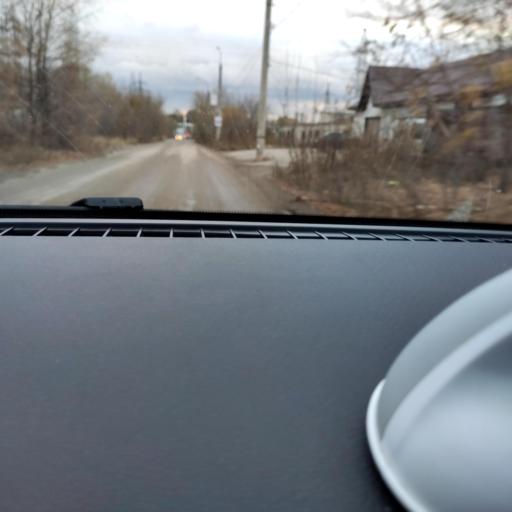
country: RU
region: Samara
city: Petra-Dubrava
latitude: 53.2597
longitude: 50.2976
